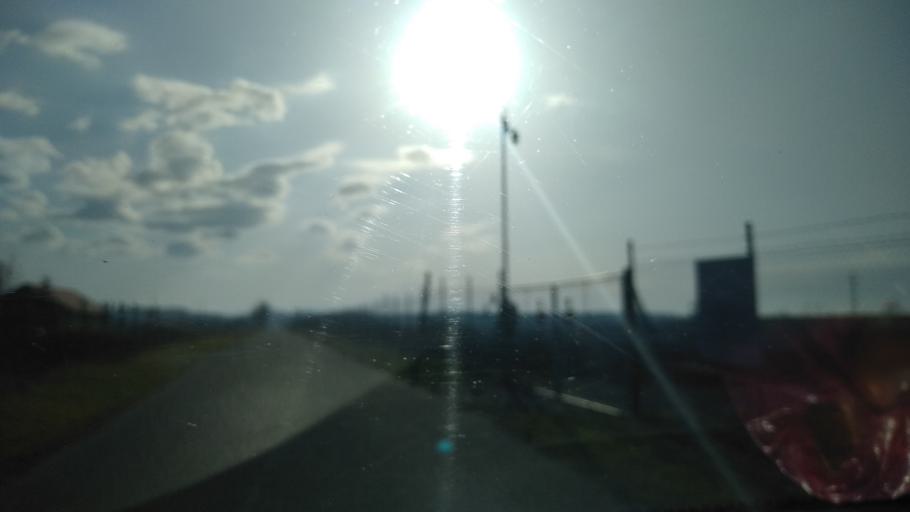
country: HU
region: Somogy
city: Barcs
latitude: 45.9734
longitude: 17.4971
